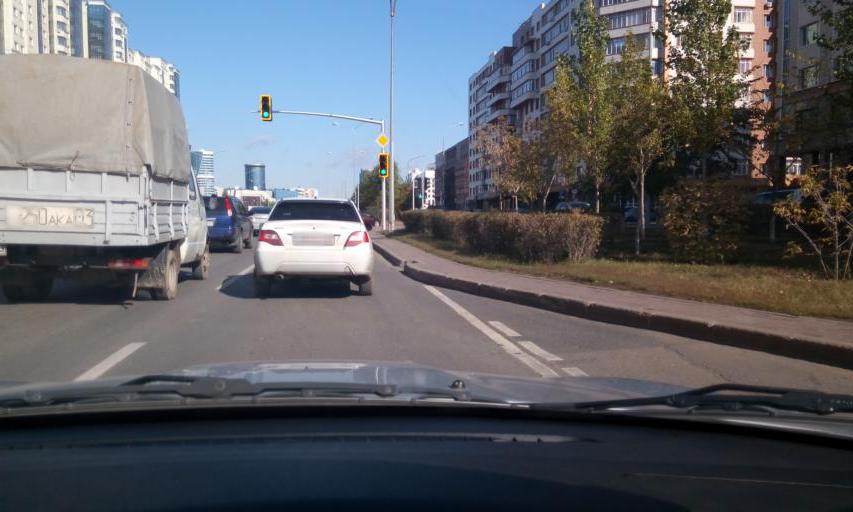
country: KZ
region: Astana Qalasy
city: Astana
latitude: 51.1147
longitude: 71.4339
